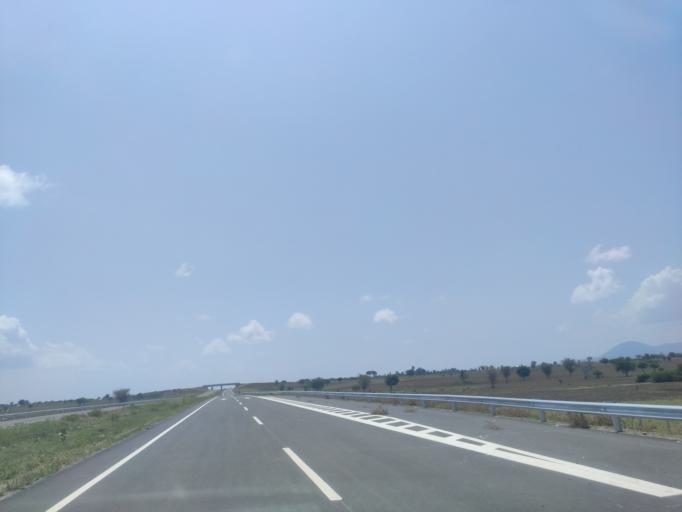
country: ET
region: Oromiya
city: Ziway
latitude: 8.2386
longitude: 38.8793
